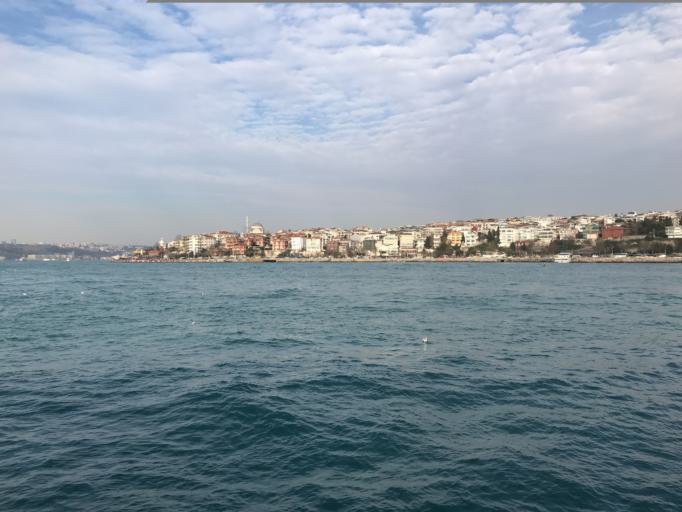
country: TR
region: Istanbul
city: UEskuedar
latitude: 41.0173
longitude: 29.0033
